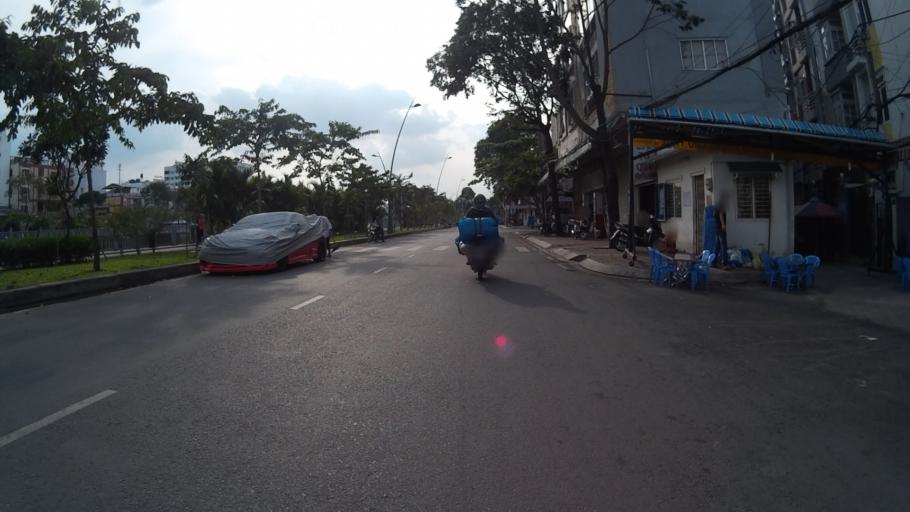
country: VN
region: Ho Chi Minh City
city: Quan Binh Thanh
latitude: 10.7961
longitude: 106.6903
